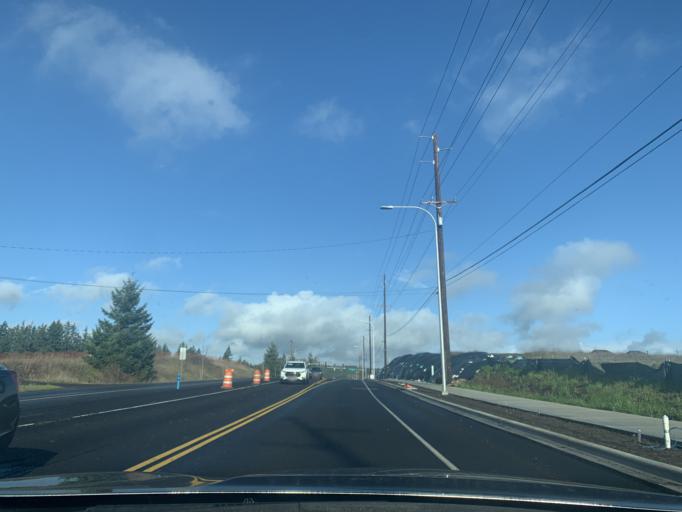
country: US
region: Oregon
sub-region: Washington County
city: King City
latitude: 45.4128
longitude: -122.8516
